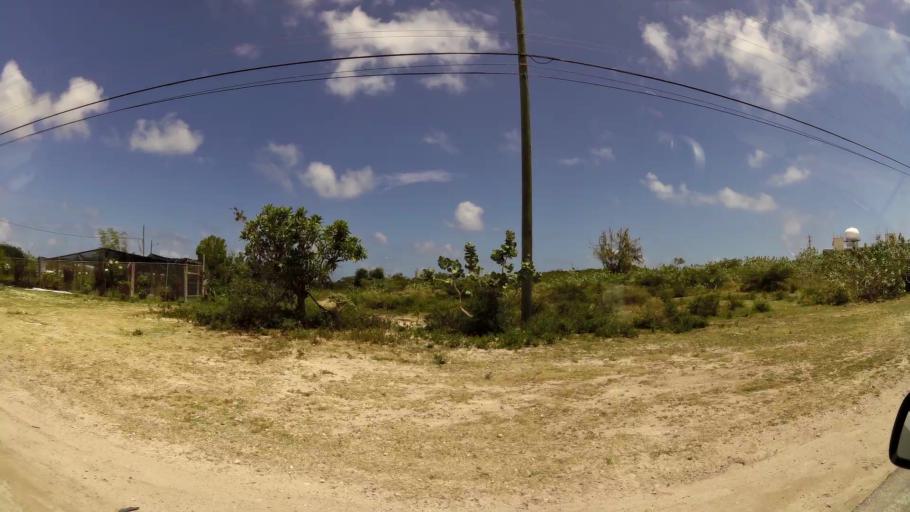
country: TC
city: Cockburn Town
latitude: 21.4355
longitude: -71.1466
